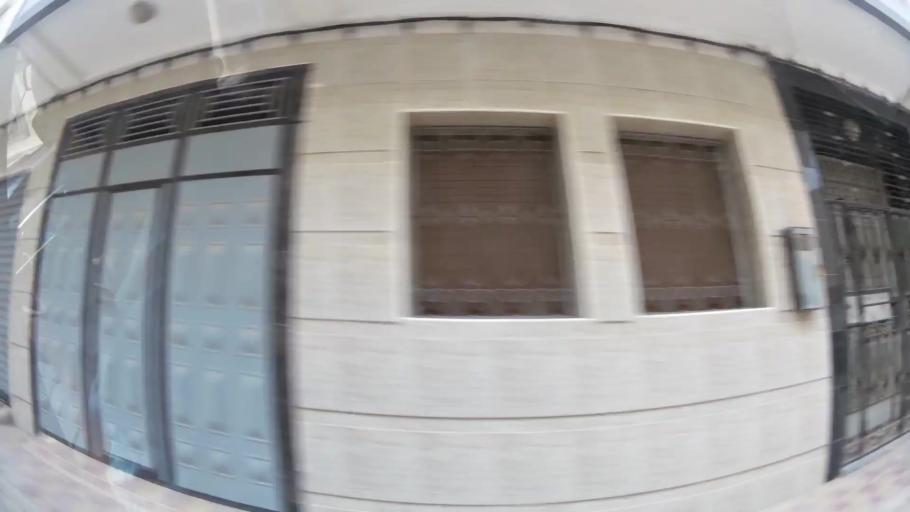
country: MA
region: Oriental
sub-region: Nador
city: Nador
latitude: 35.1643
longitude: -2.9345
